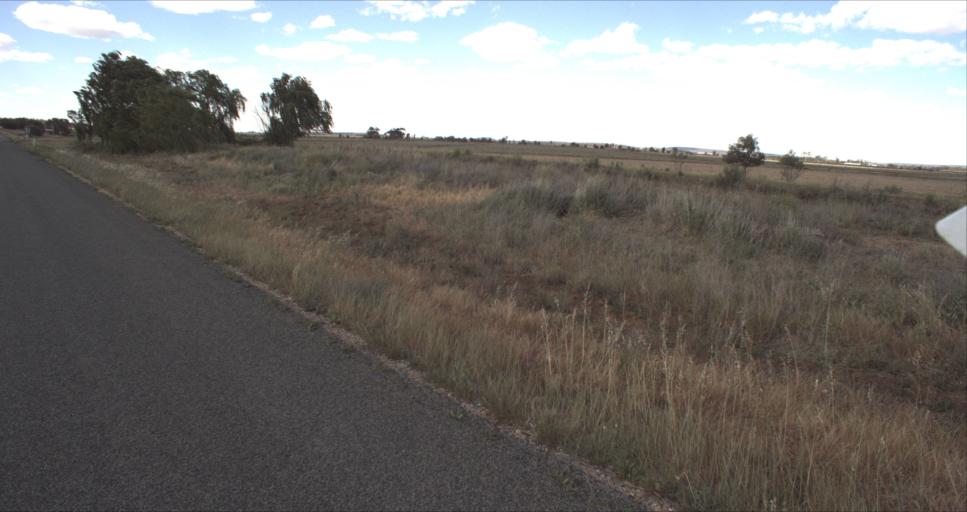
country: AU
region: New South Wales
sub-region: Leeton
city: Leeton
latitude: -34.4452
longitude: 146.2556
